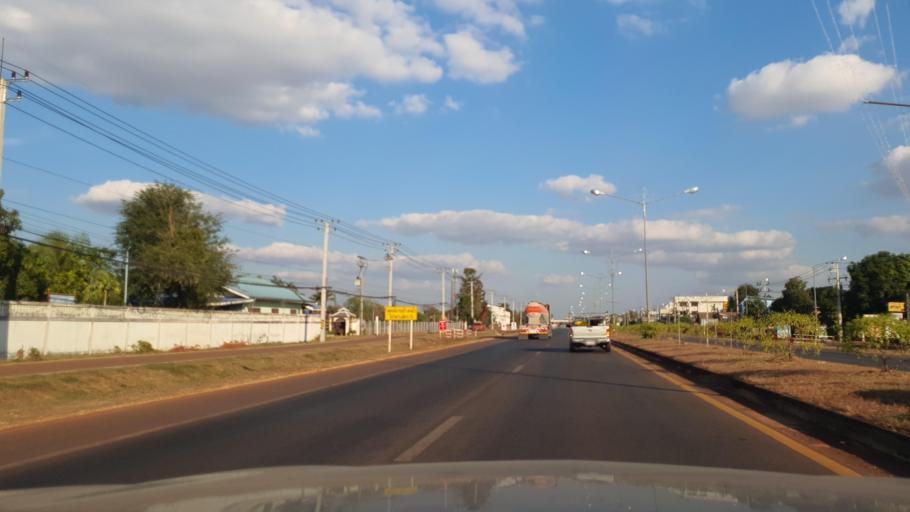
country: TH
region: Sakon Nakhon
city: Sakon Nakhon
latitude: 17.2565
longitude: 104.1773
